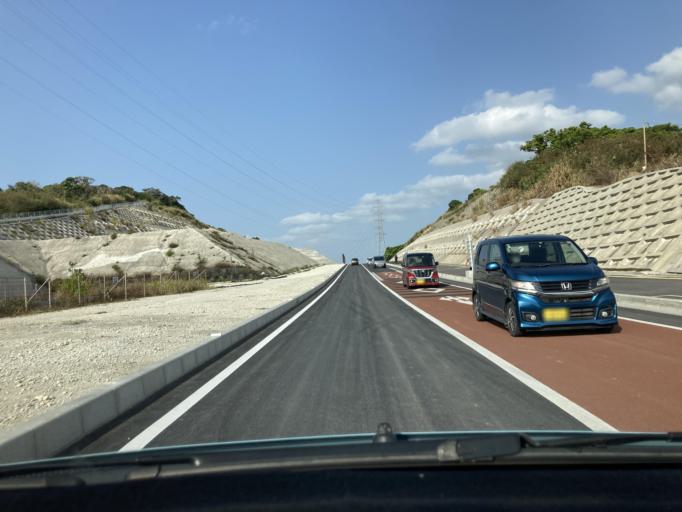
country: JP
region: Okinawa
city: Ginowan
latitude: 26.2044
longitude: 127.7490
